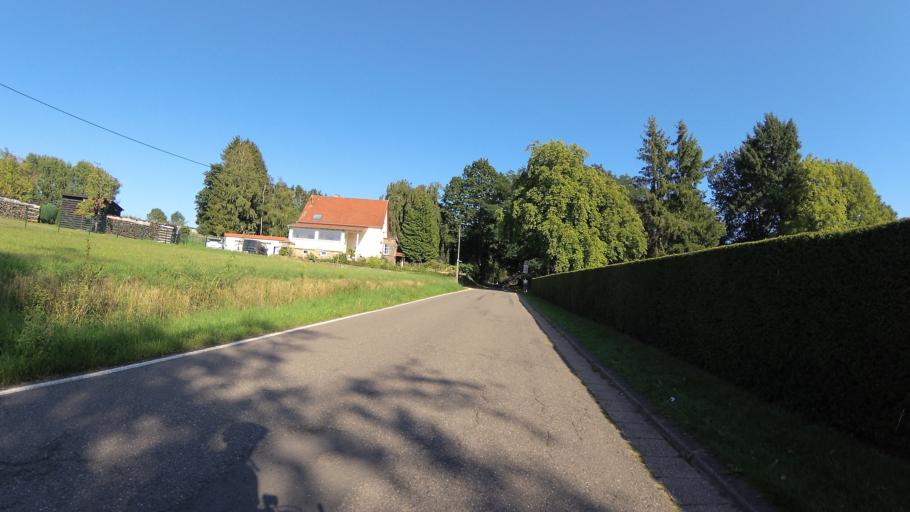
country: DE
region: Saarland
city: Weiskirchen
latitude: 49.5578
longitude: 6.8370
